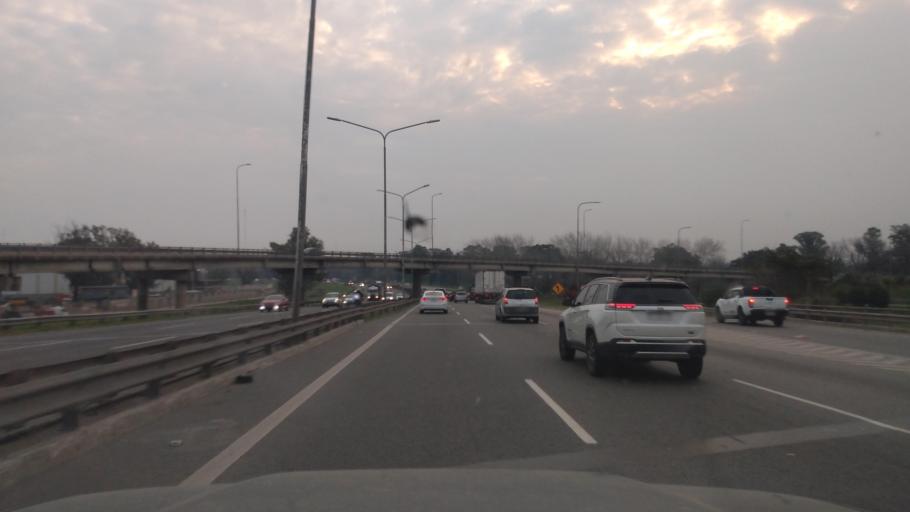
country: AR
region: Buenos Aires
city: Hurlingham
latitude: -34.5689
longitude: -58.6532
